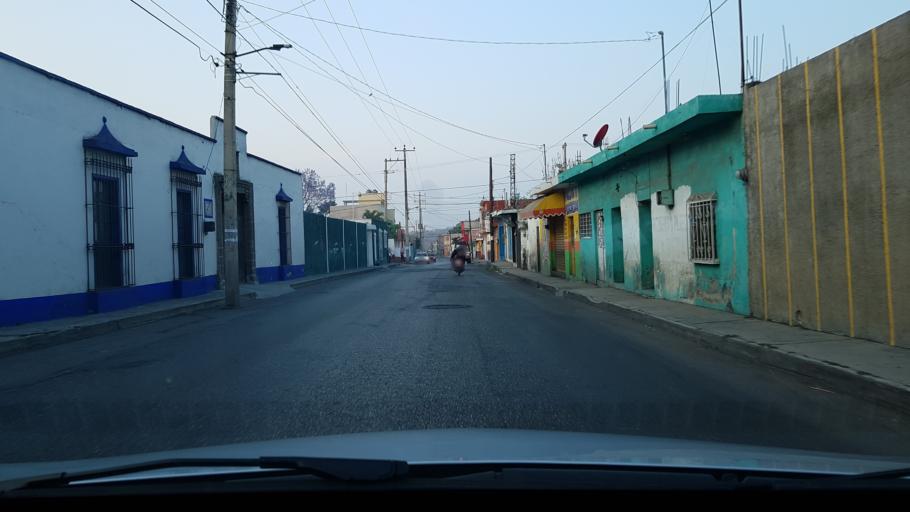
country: MX
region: Morelos
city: Jonacatepec de Leandro Valle
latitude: 18.6842
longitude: -98.8030
